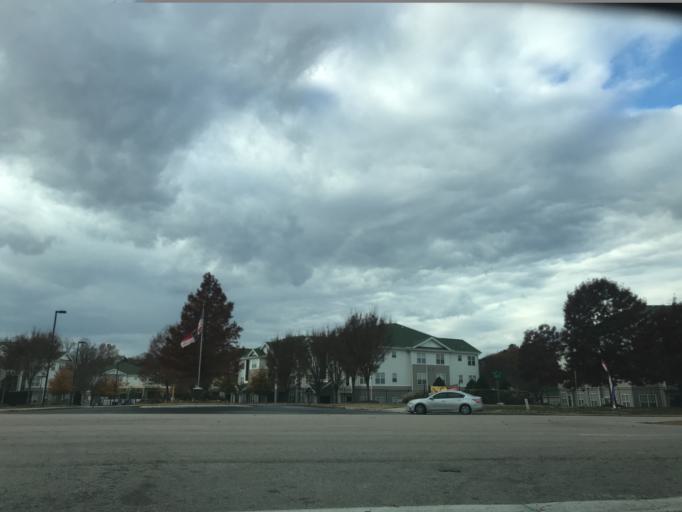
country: US
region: North Carolina
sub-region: Wake County
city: Raleigh
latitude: 35.8474
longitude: -78.5864
